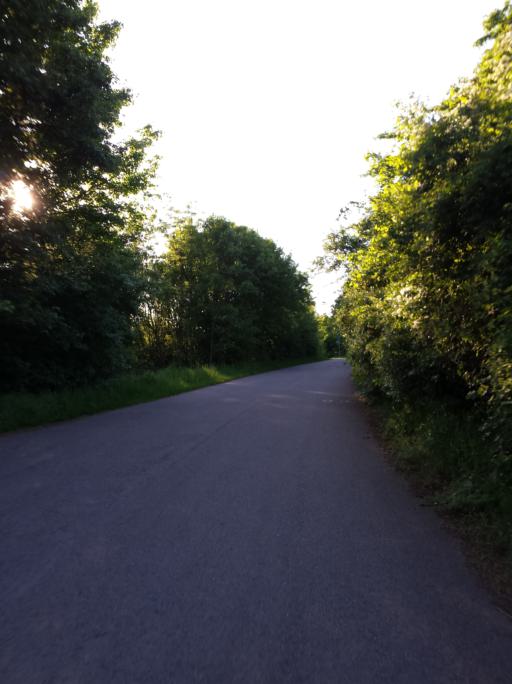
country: AT
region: Vienna
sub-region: Wien Stadt
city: Vienna
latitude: 48.2113
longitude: 16.4323
